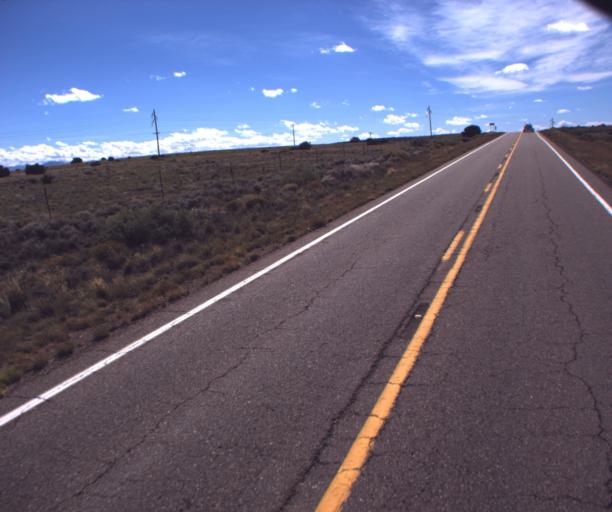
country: US
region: Arizona
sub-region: Apache County
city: Saint Johns
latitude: 34.4961
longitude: -109.5085
